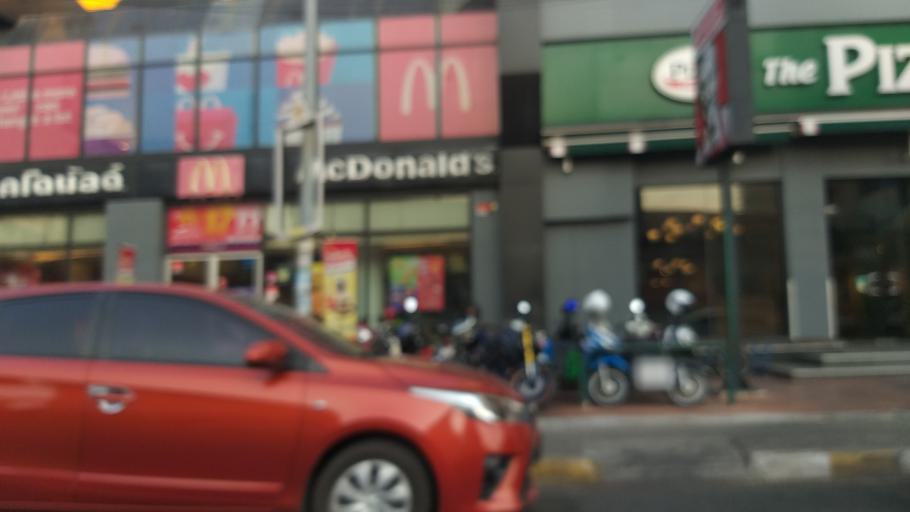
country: TH
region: Khon Kaen
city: Khon Kaen
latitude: 16.4237
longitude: 102.8333
